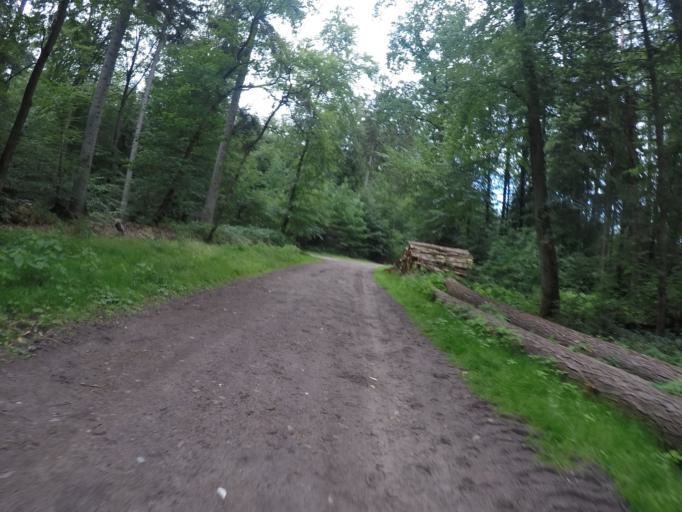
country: DE
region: Lower Saxony
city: Wingst
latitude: 53.7313
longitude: 9.0693
